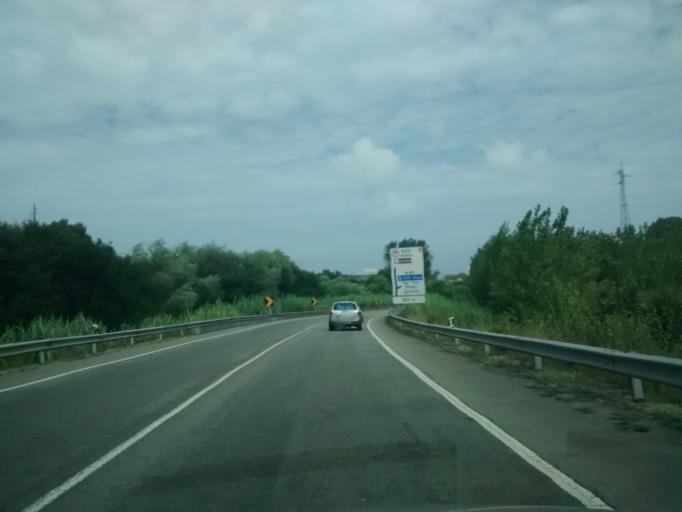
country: PT
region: Aveiro
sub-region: Aveiro
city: Aradas
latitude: 40.6206
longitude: -8.6441
